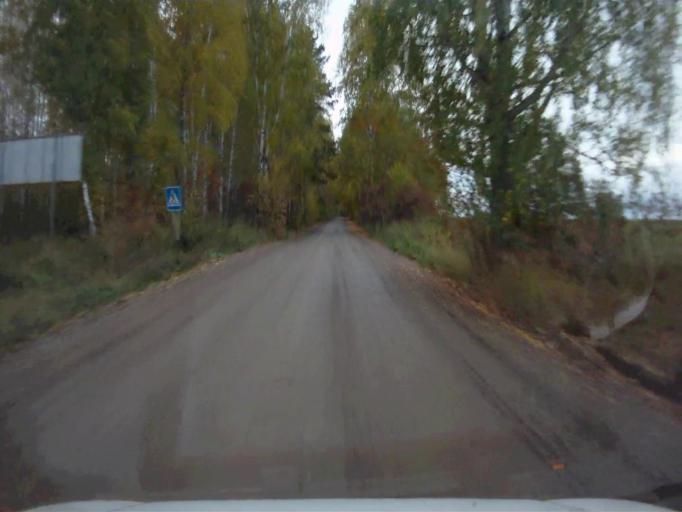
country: RU
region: Sverdlovsk
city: Mikhaylovsk
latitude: 56.1693
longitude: 59.2266
